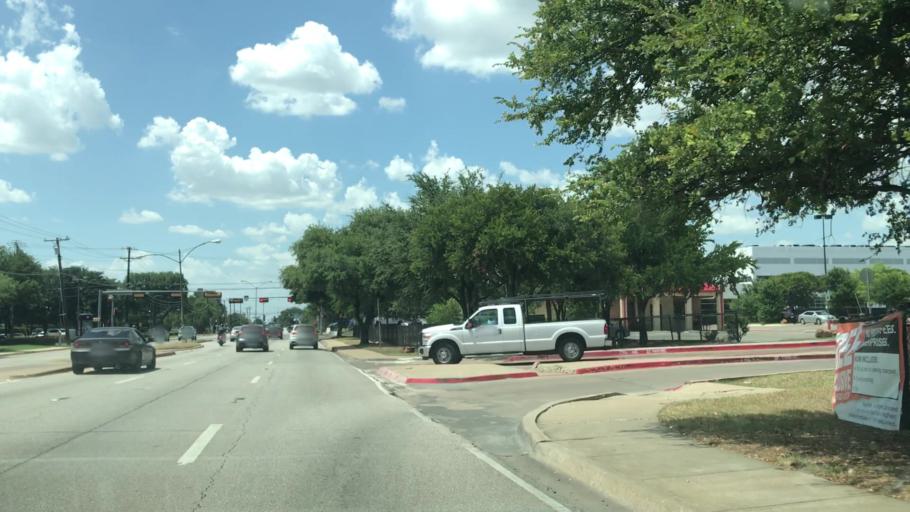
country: US
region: Texas
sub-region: Dallas County
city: University Park
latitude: 32.8329
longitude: -96.8288
